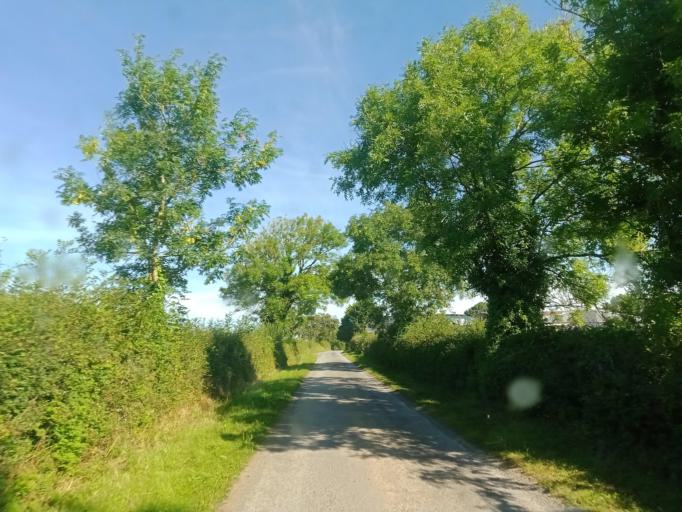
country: IE
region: Leinster
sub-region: Kilkenny
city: Ballyragget
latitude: 52.7909
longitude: -7.4237
